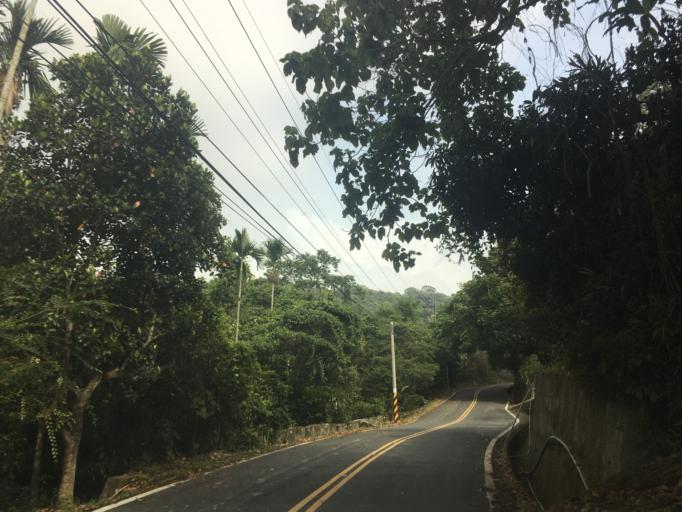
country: TW
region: Taiwan
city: Fengyuan
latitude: 24.2228
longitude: 120.7605
